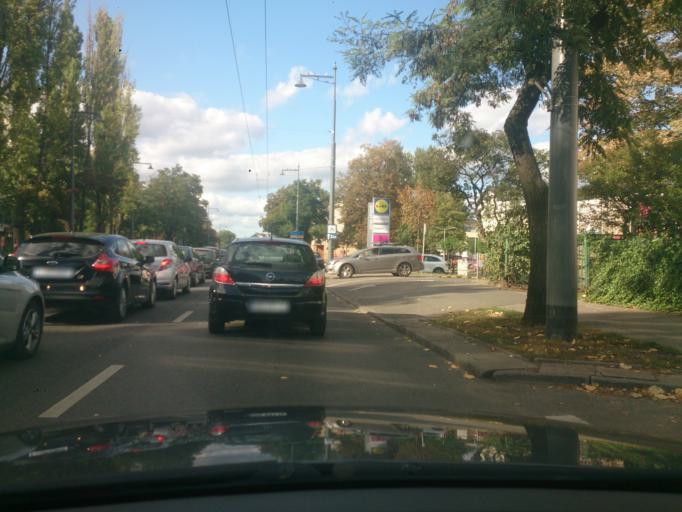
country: PL
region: Pomeranian Voivodeship
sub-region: Sopot
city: Sopot
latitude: 54.4326
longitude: 18.5618
